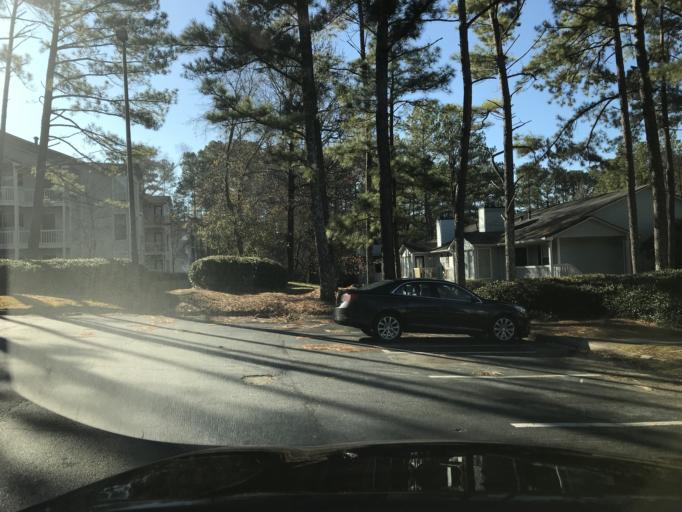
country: US
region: Georgia
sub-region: Clayton County
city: Riverdale
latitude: 33.5647
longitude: -84.3751
